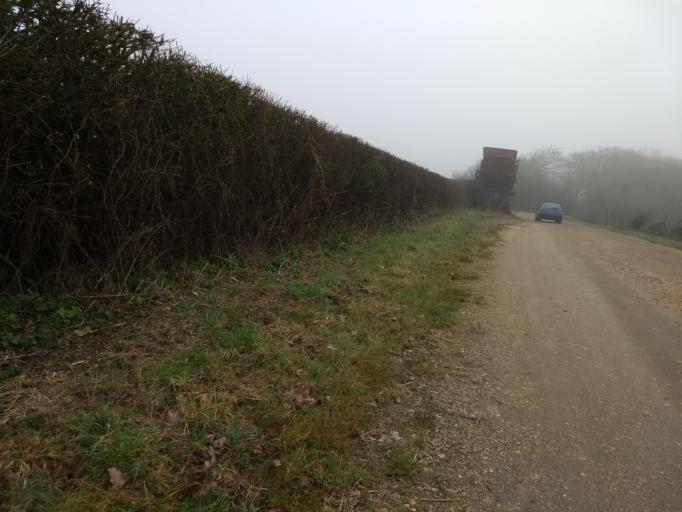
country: GB
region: England
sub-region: Isle of Wight
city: Newport
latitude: 50.7014
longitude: -1.2639
